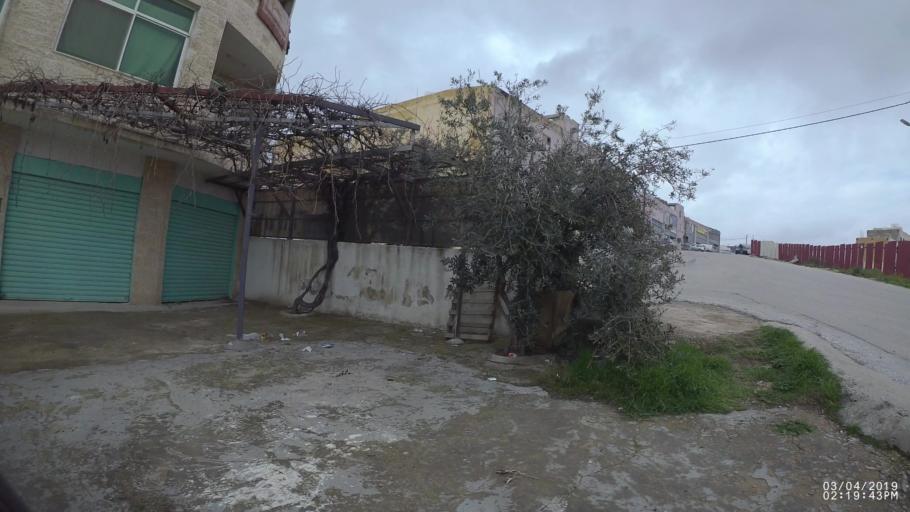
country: JO
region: Amman
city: Wadi as Sir
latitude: 31.9403
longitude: 35.8339
